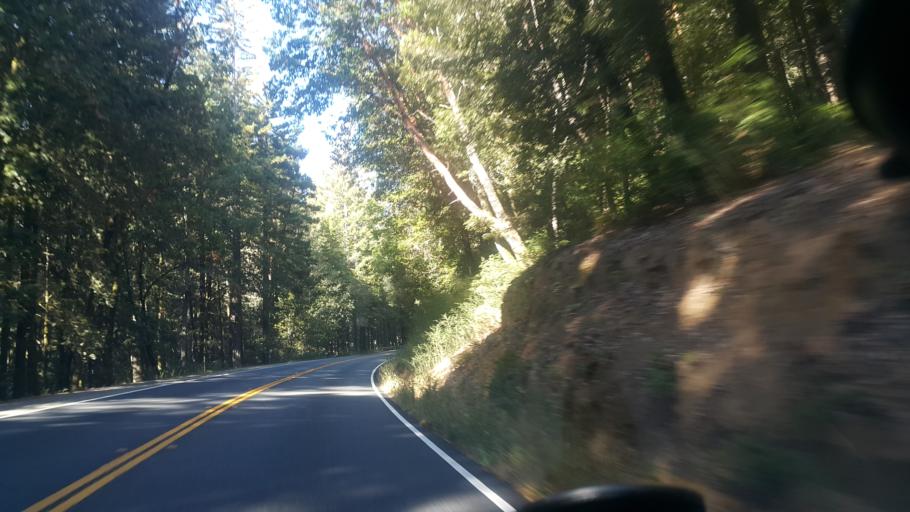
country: US
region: California
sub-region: Mendocino County
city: Fort Bragg
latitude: 39.3630
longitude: -123.6671
